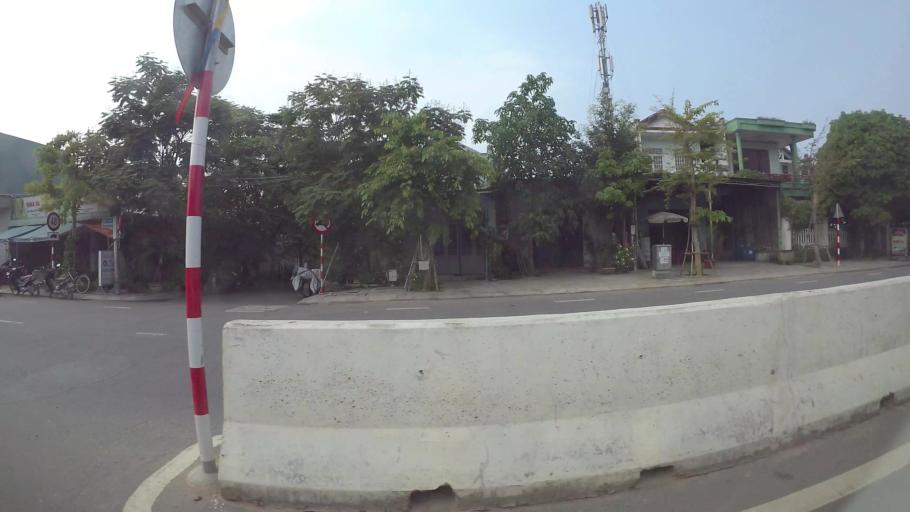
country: VN
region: Da Nang
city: Lien Chieu
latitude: 16.0486
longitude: 108.1466
